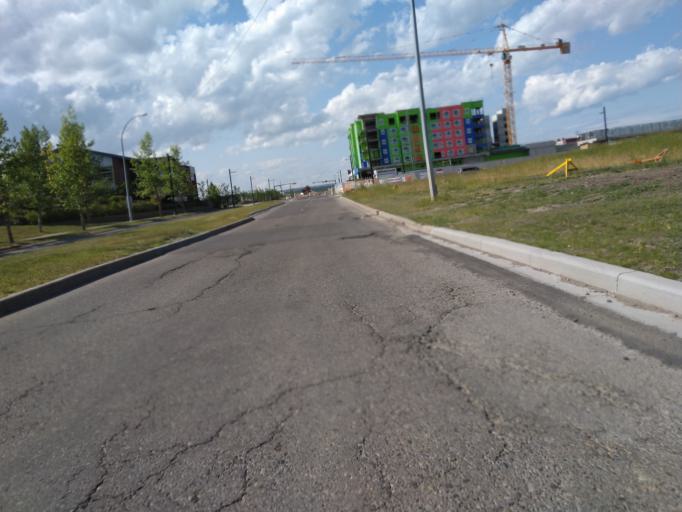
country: CA
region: Alberta
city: Calgary
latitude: 51.0757
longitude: -114.1459
